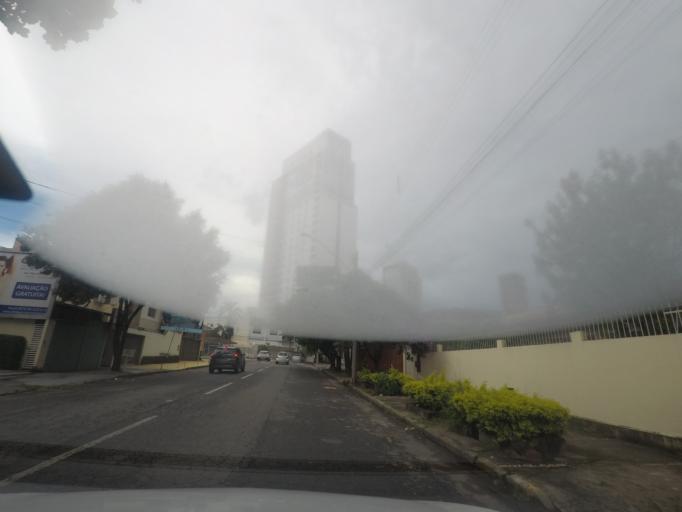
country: BR
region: Goias
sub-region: Goiania
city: Goiania
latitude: -16.7004
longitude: -49.2651
